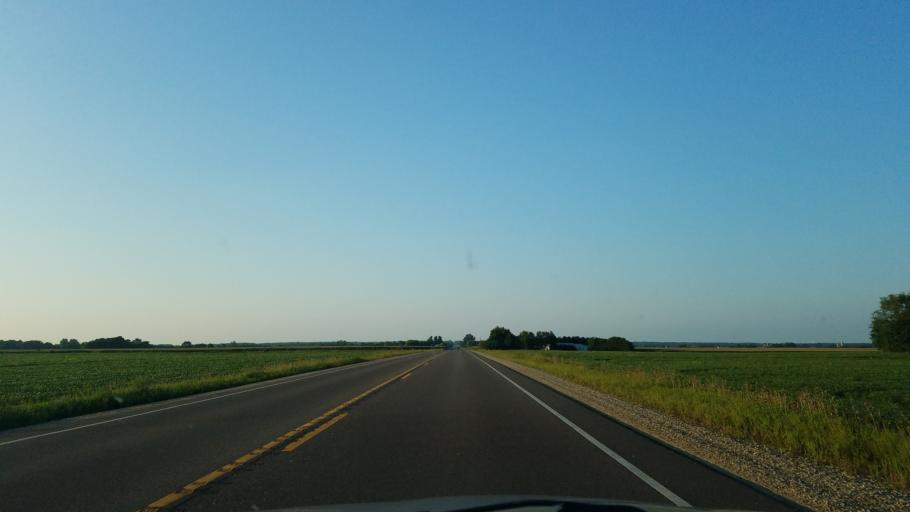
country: US
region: Wisconsin
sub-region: Polk County
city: Clear Lake
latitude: 45.2059
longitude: -92.2838
